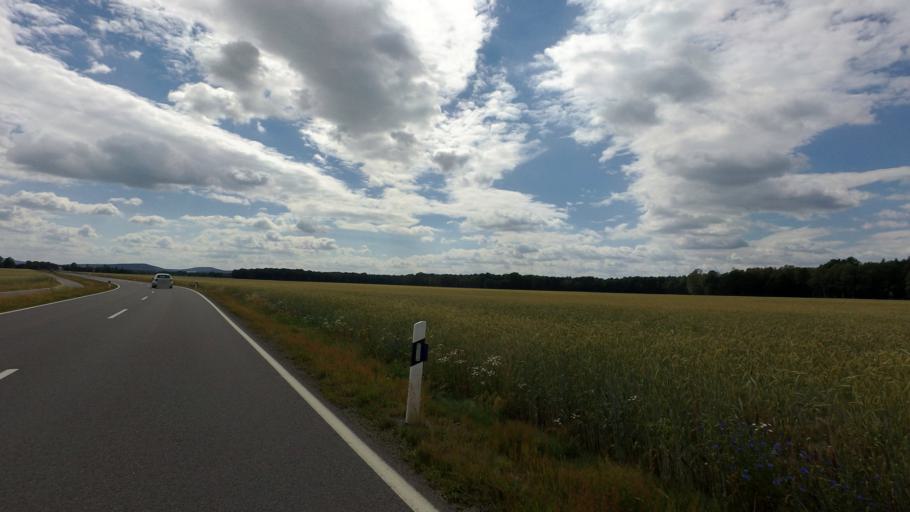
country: DE
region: Saxony
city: Ossling
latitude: 51.3214
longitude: 14.1458
